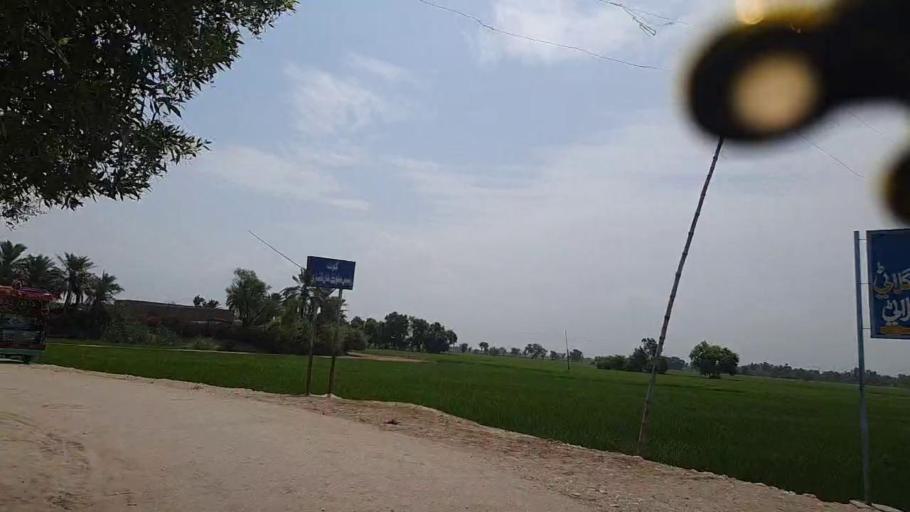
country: PK
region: Sindh
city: Rustam jo Goth
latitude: 28.1108
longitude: 68.8607
